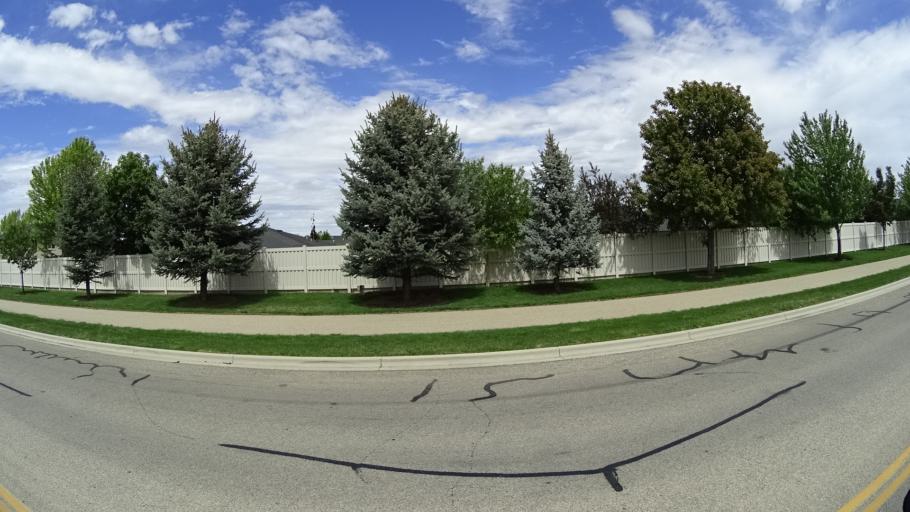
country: US
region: Idaho
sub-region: Ada County
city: Meridian
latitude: 43.5762
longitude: -116.3974
